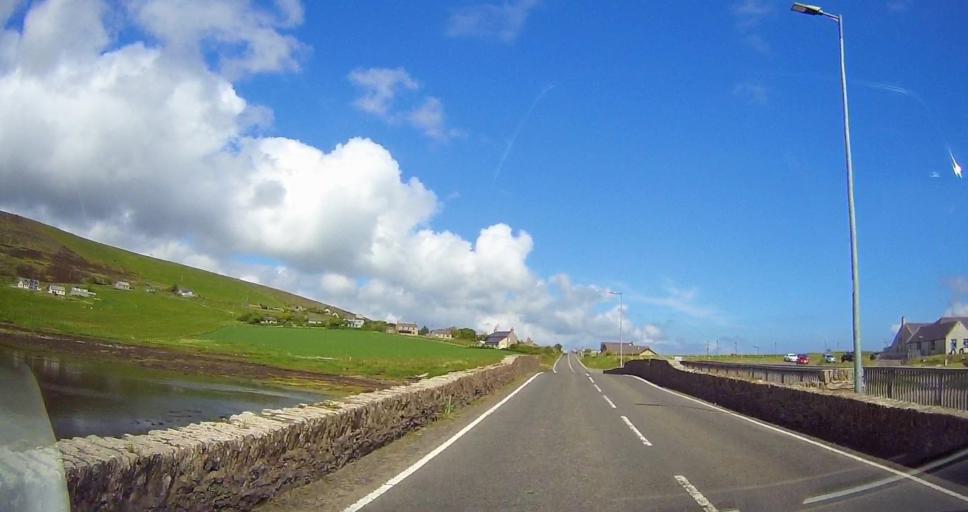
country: GB
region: Scotland
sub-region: Orkney Islands
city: Orkney
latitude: 59.0102
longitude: -3.1134
